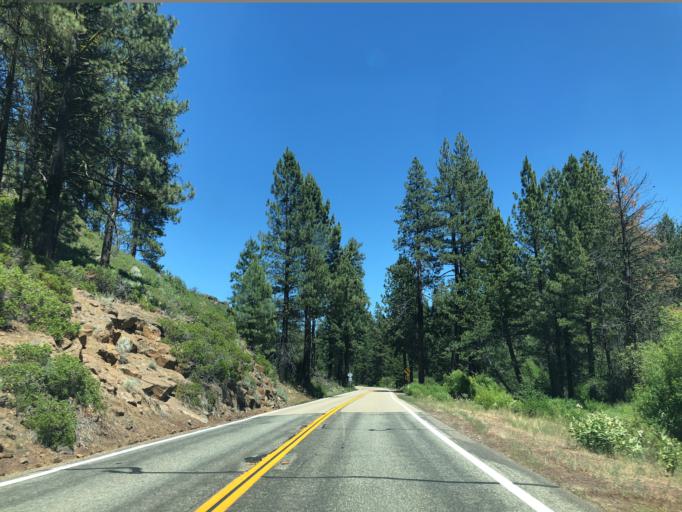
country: US
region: California
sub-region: Shasta County
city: Burney
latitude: 40.6436
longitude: -121.4700
